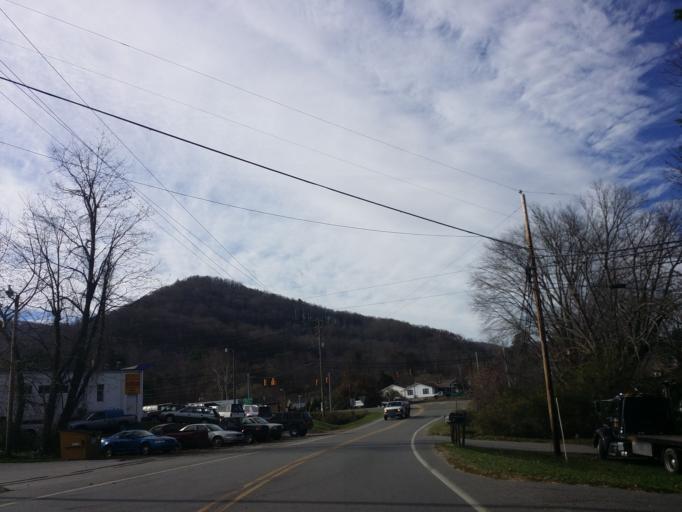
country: US
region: North Carolina
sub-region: Buncombe County
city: Swannanoa
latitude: 35.5999
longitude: -82.4088
